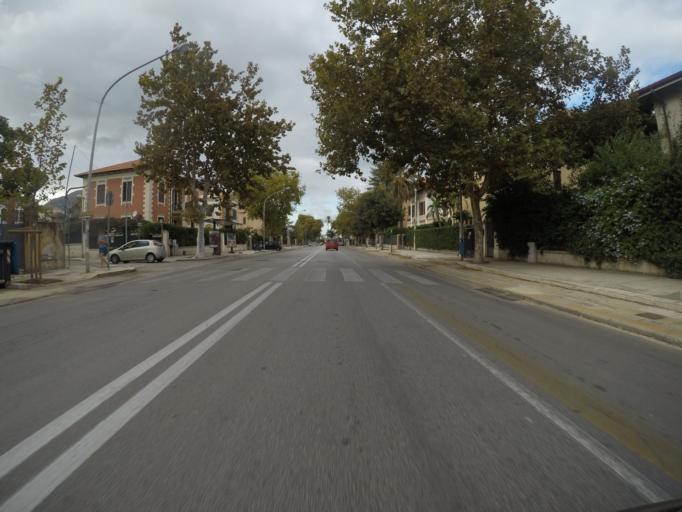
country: IT
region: Sicily
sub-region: Palermo
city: Palermo
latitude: 38.1952
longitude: 13.3321
